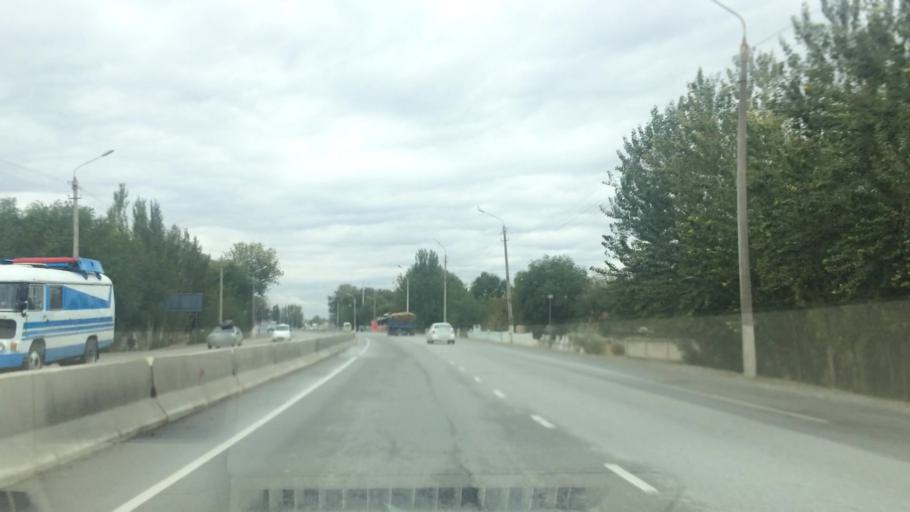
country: UZ
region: Jizzax
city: Jizzax
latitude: 39.9870
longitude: 67.5773
